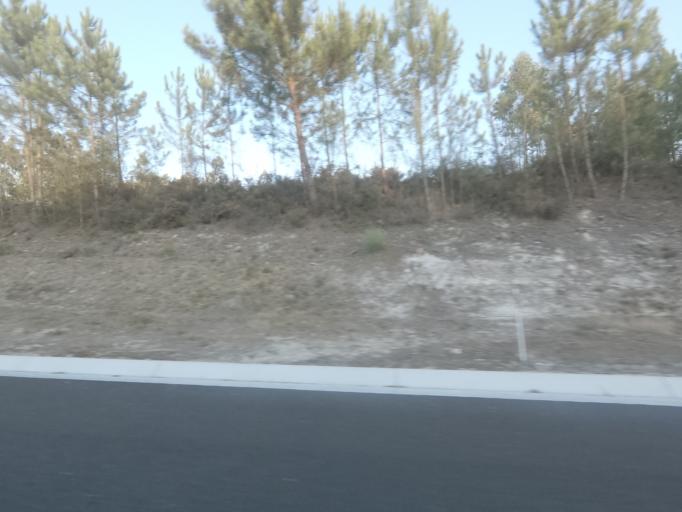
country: PT
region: Leiria
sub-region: Leiria
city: Caranguejeira
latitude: 39.7796
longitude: -8.7389
